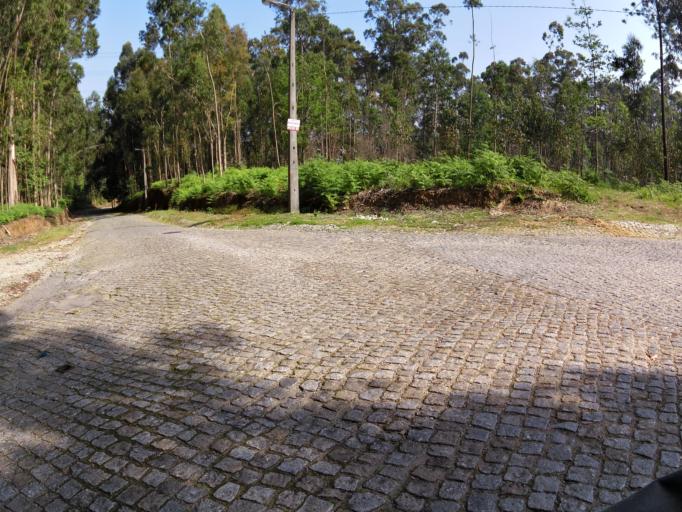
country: PT
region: Porto
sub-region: Vila Nova de Gaia
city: Olival
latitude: 41.0419
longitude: -8.5346
